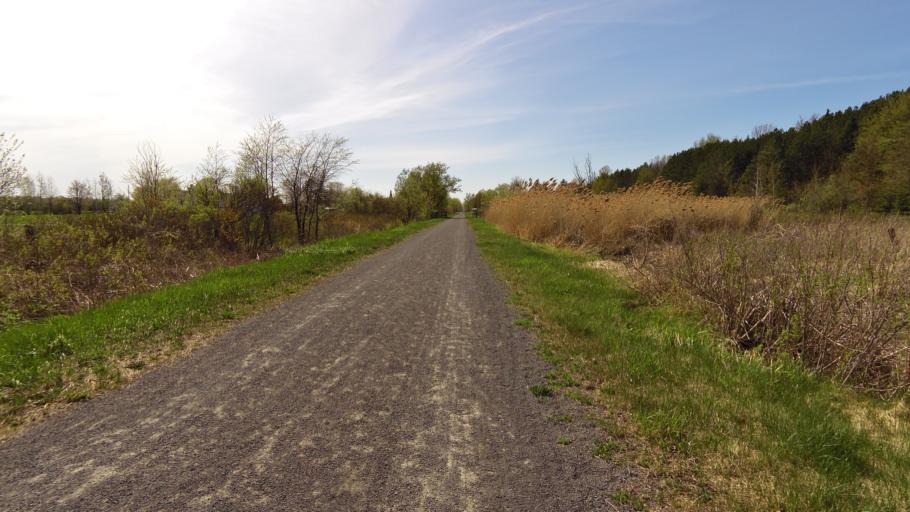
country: CA
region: Ontario
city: Clarence-Rockland
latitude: 45.4175
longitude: -75.4599
